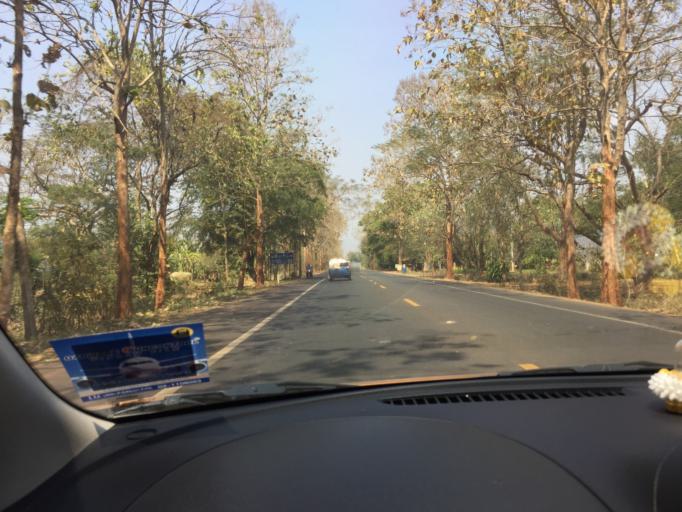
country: TH
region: Kanchanaburi
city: Sai Yok
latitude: 14.1703
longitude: 99.1313
